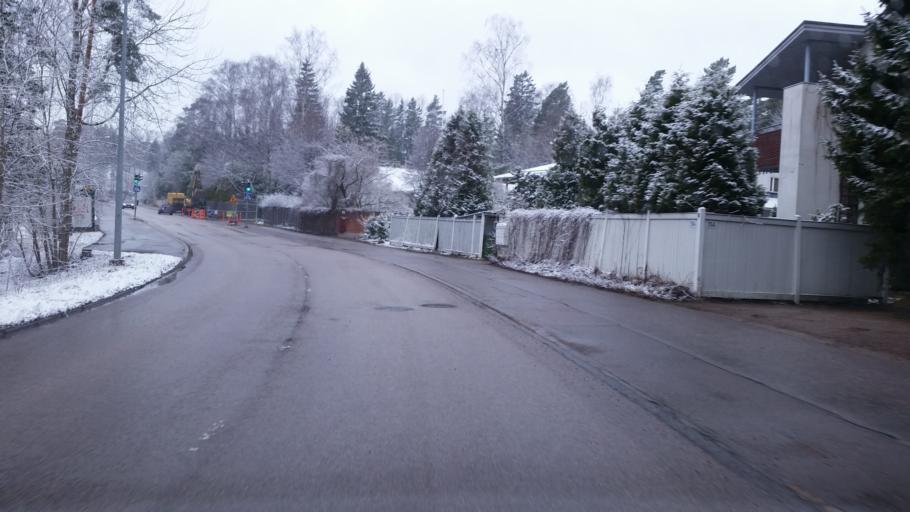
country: FI
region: Uusimaa
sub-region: Helsinki
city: Koukkuniemi
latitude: 60.1644
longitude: 24.7952
